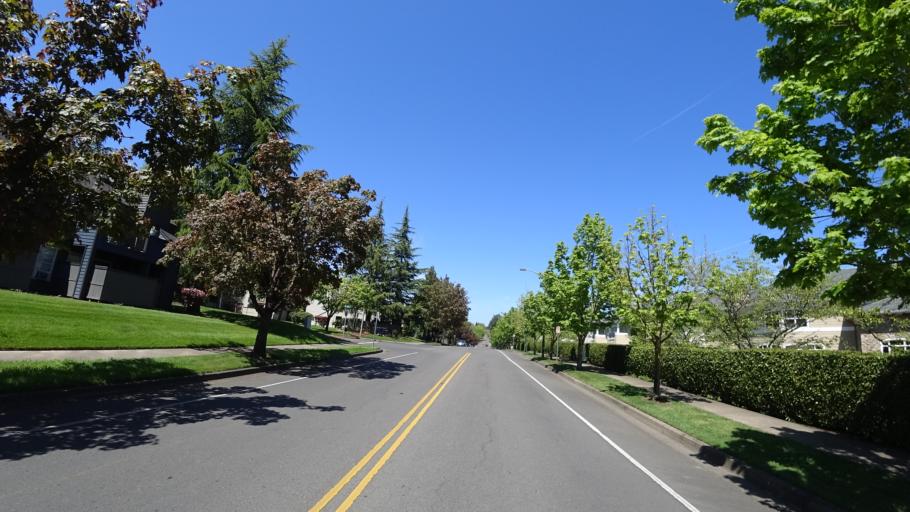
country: US
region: Oregon
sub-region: Washington County
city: King City
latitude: 45.4411
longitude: -122.8209
